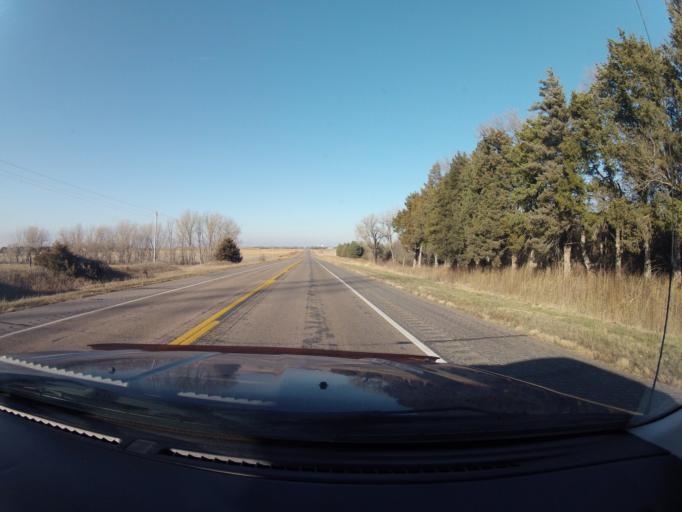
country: US
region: Nebraska
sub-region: Kearney County
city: Minden
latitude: 40.5763
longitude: -98.9519
